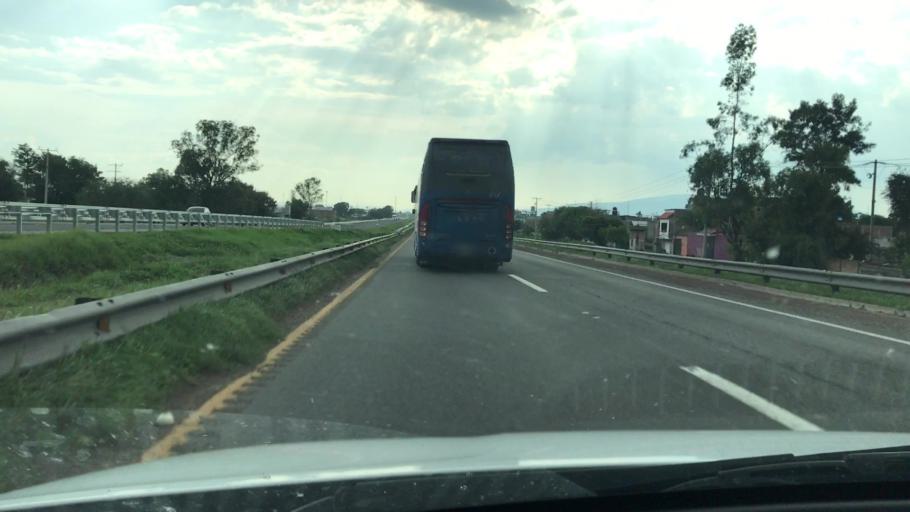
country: MX
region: Guanajuato
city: Irapuato
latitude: 20.6494
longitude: -101.3601
